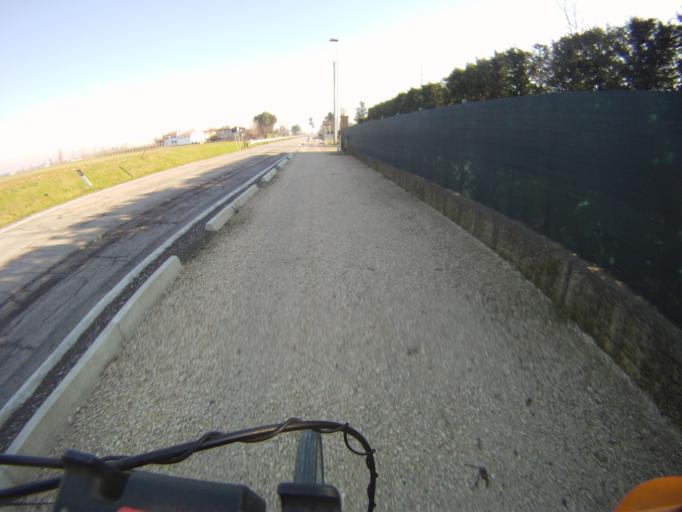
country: IT
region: Veneto
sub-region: Provincia di Padova
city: Brugine
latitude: 45.3125
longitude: 11.9765
